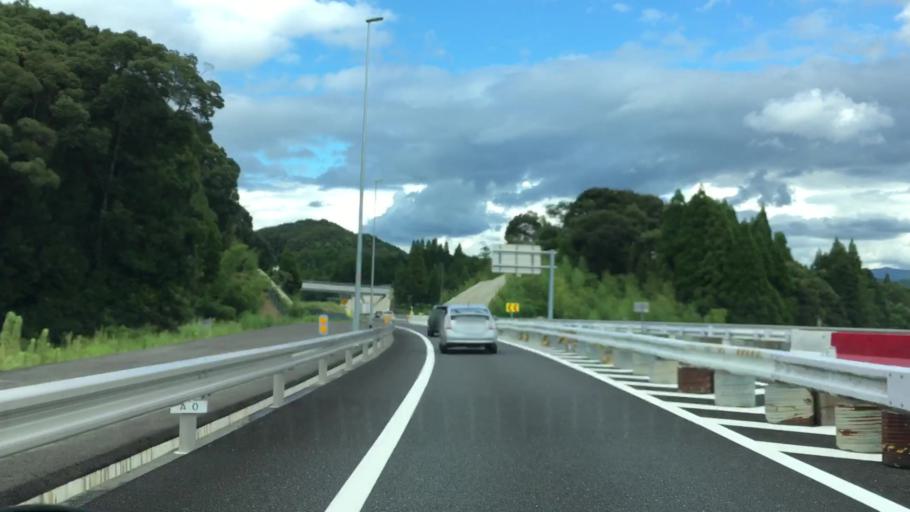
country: JP
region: Saga Prefecture
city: Imaricho-ko
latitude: 33.2984
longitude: 129.9136
